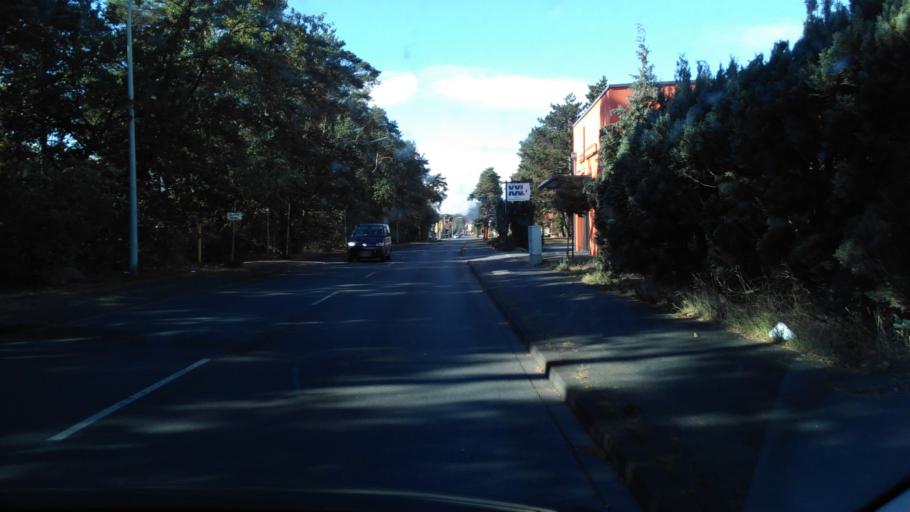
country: DE
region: North Rhine-Westphalia
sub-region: Regierungsbezirk Detmold
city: Oerlinghausen
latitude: 51.9017
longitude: 8.6273
